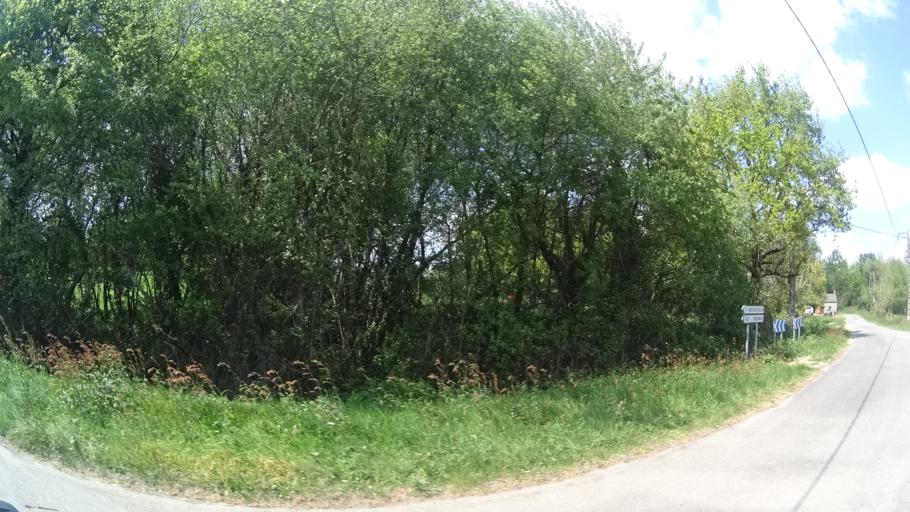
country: FR
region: Brittany
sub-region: Departement du Morbihan
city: Allaire
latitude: 47.6005
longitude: -2.1732
